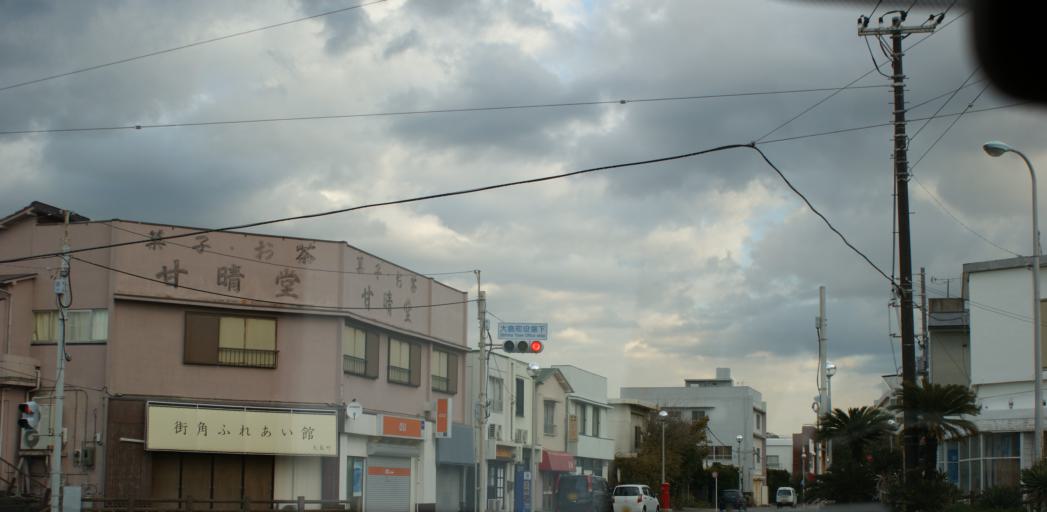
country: JP
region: Shizuoka
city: Ito
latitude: 34.7497
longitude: 139.3547
